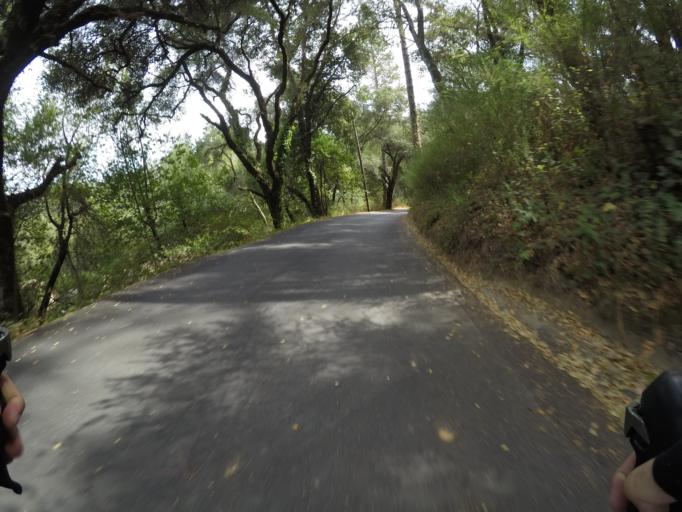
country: US
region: California
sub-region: Santa Cruz County
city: Mount Hermon
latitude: 37.0566
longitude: -122.0620
